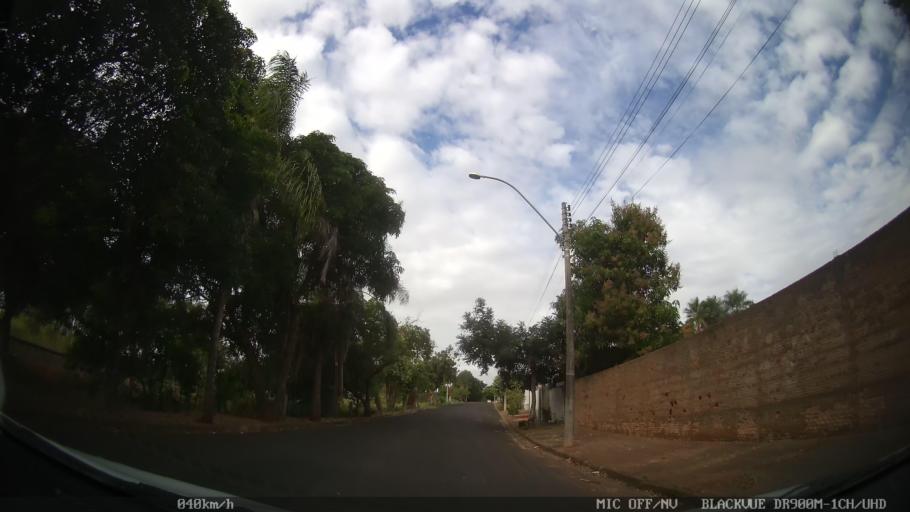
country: BR
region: Sao Paulo
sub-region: Sao Jose Do Rio Preto
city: Sao Jose do Rio Preto
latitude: -20.8217
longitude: -49.3488
